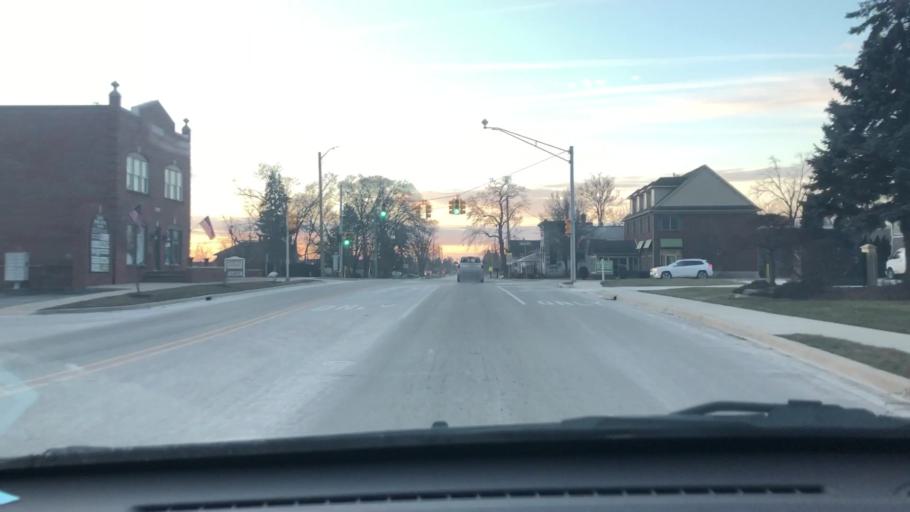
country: US
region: Michigan
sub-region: Macomb County
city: Shelby
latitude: 42.7251
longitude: -83.0359
